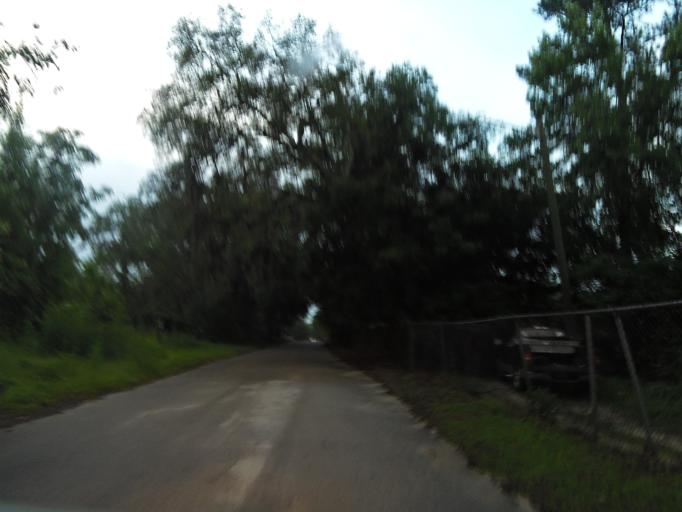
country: US
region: Florida
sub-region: Duval County
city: Jacksonville
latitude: 30.2697
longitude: -81.6396
